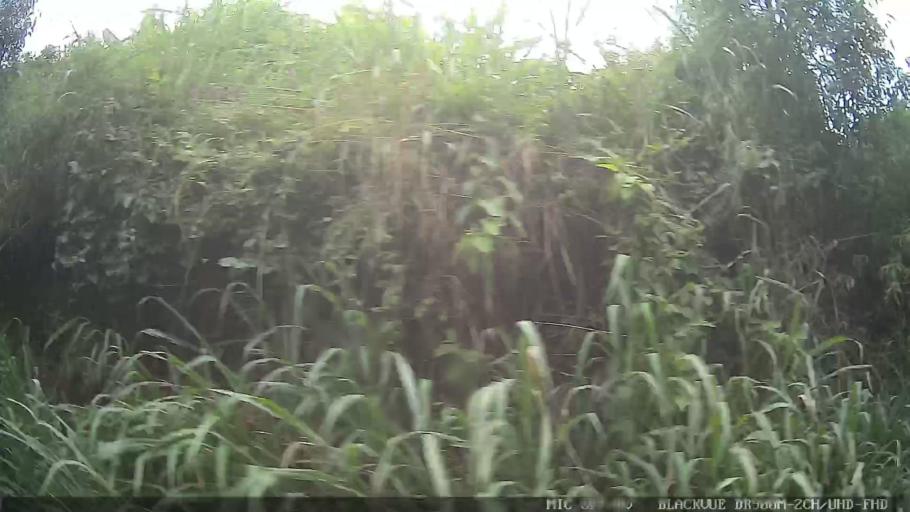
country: BR
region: Sao Paulo
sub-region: Atibaia
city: Atibaia
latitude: -23.1094
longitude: -46.6079
